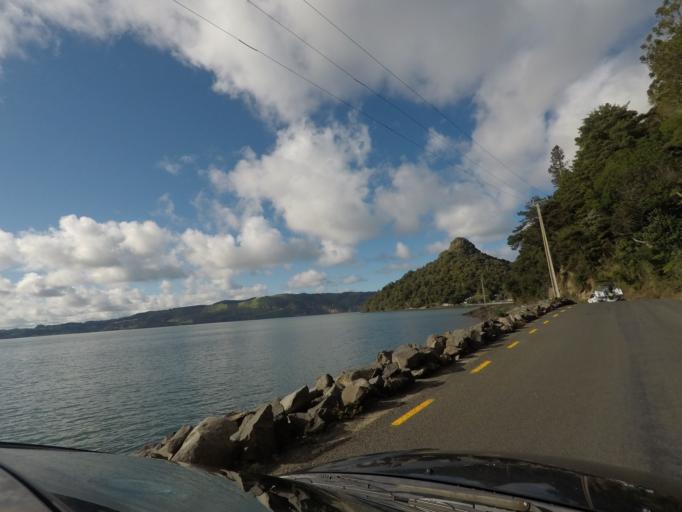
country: NZ
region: Auckland
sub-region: Auckland
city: Titirangi
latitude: -37.0123
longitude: 174.5611
